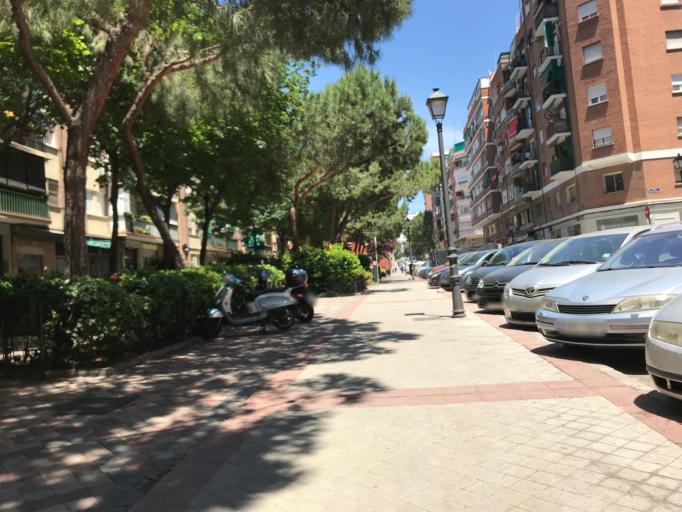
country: ES
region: Madrid
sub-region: Provincia de Madrid
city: Arganzuela
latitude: 40.3956
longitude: -3.7000
